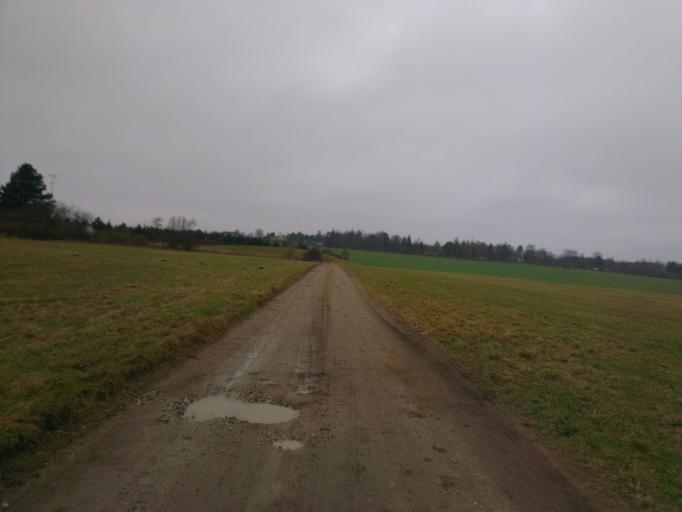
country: DK
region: Capital Region
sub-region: Frederikssund Kommune
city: Jaegerspris
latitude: 55.8438
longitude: 12.0052
